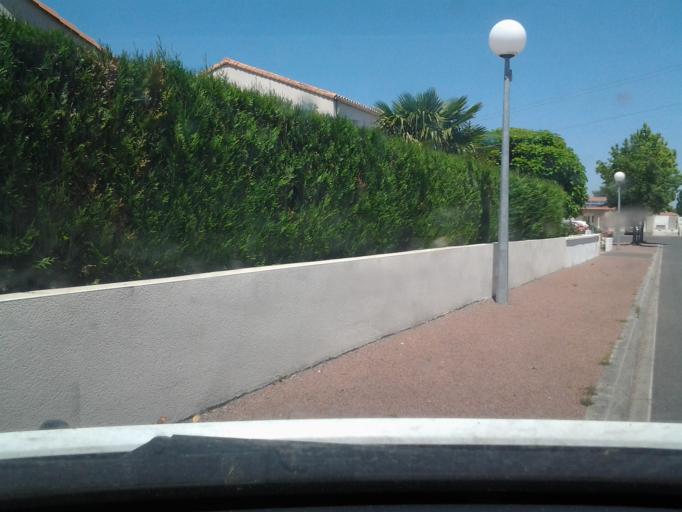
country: FR
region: Pays de la Loire
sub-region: Departement de la Vendee
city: La Roche-sur-Yon
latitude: 46.6567
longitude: -1.4517
